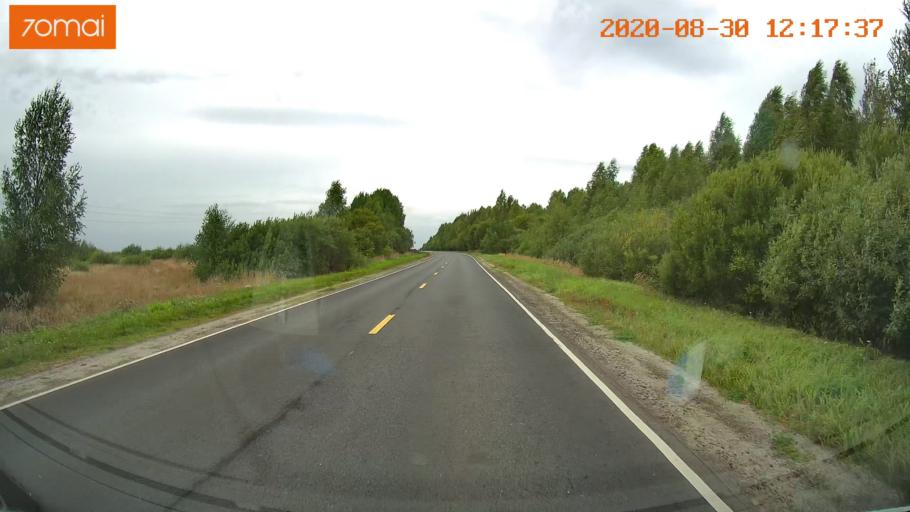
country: RU
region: Ivanovo
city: Yur'yevets
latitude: 57.3237
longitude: 42.9734
